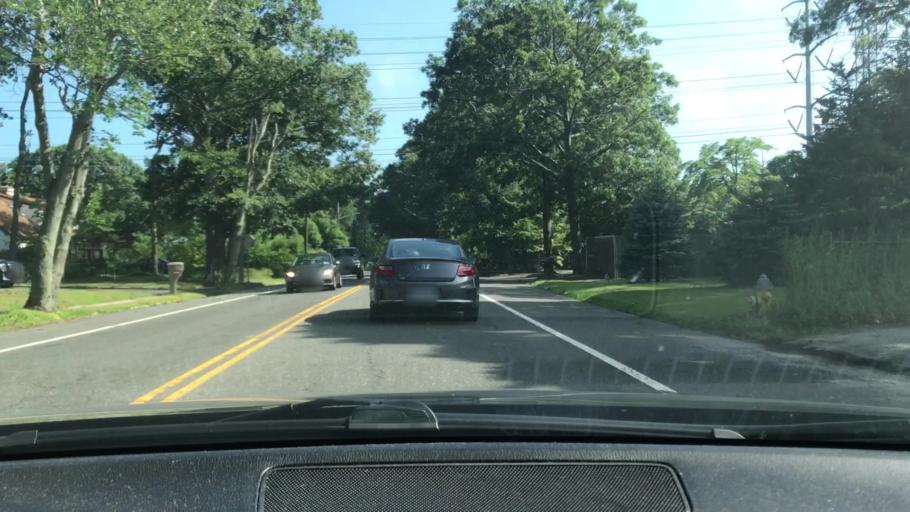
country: US
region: New York
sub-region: Suffolk County
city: Holbrook
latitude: 40.8202
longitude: -73.0798
